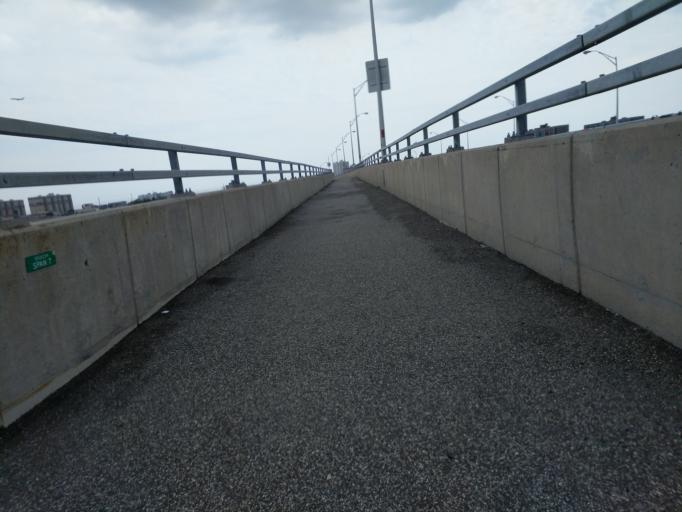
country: US
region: New York
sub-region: Nassau County
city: Inwood
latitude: 40.5918
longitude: -73.8196
